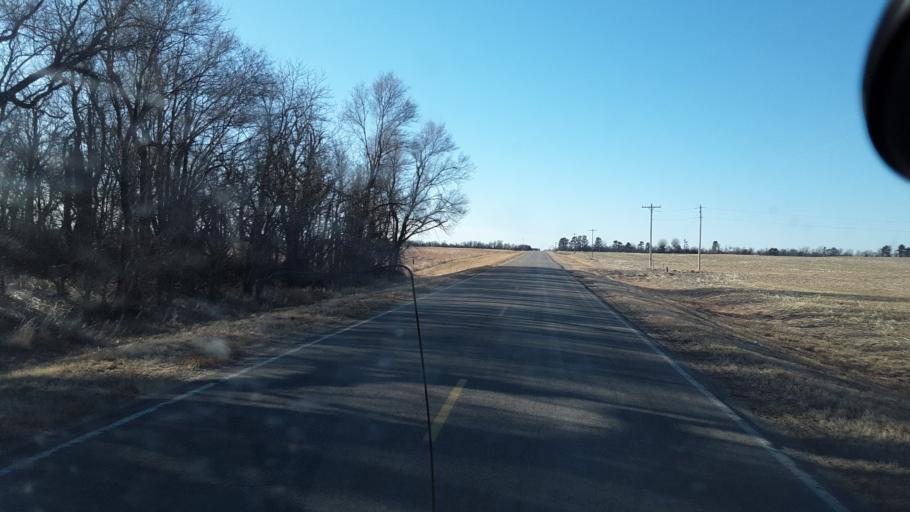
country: US
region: Kansas
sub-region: Barton County
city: Ellinwood
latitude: 38.3255
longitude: -98.6642
